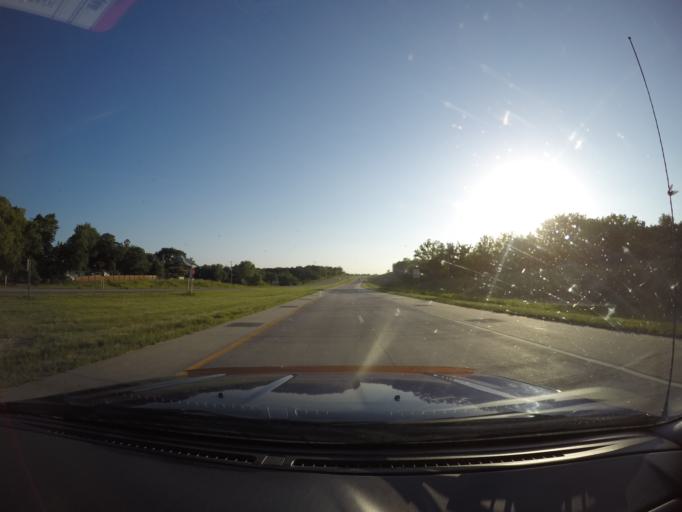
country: US
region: Kansas
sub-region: Riley County
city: Manhattan
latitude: 39.2000
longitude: -96.4452
